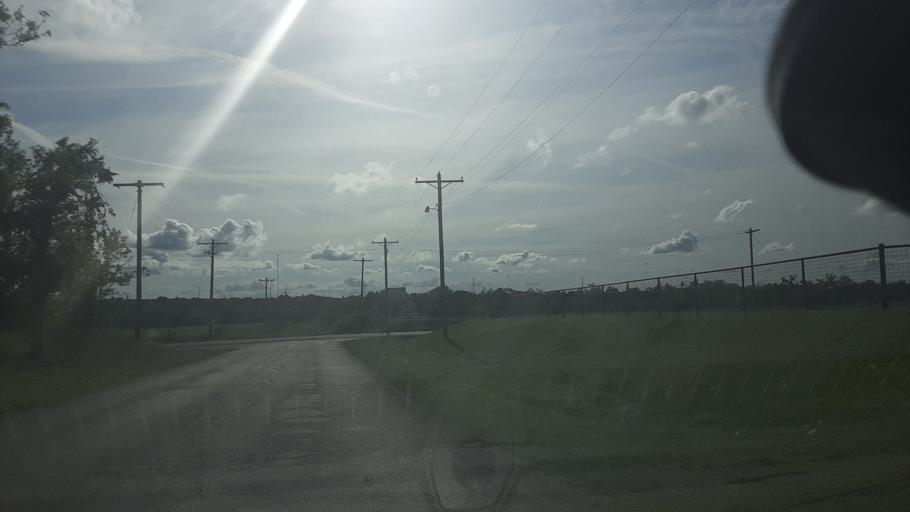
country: US
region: Oklahoma
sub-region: Logan County
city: Guthrie
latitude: 36.0576
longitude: -97.4071
